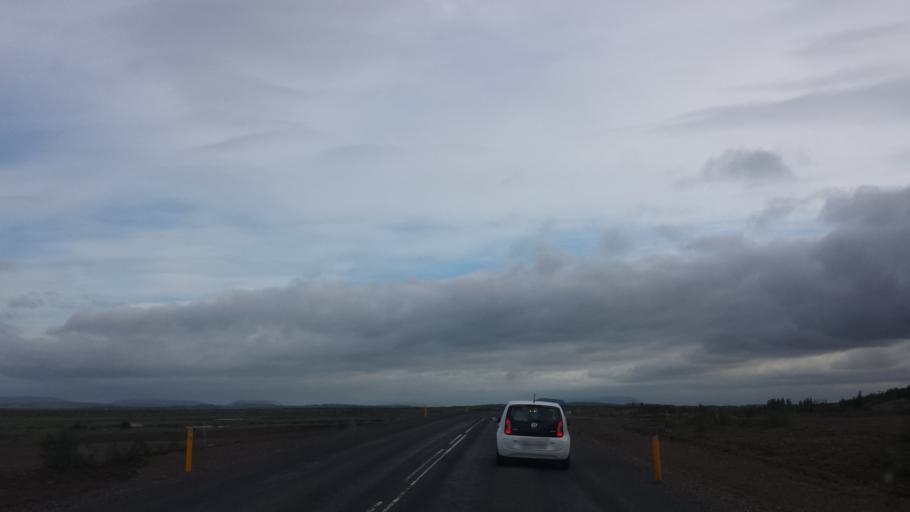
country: IS
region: South
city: Selfoss
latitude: 64.2866
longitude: -20.3400
